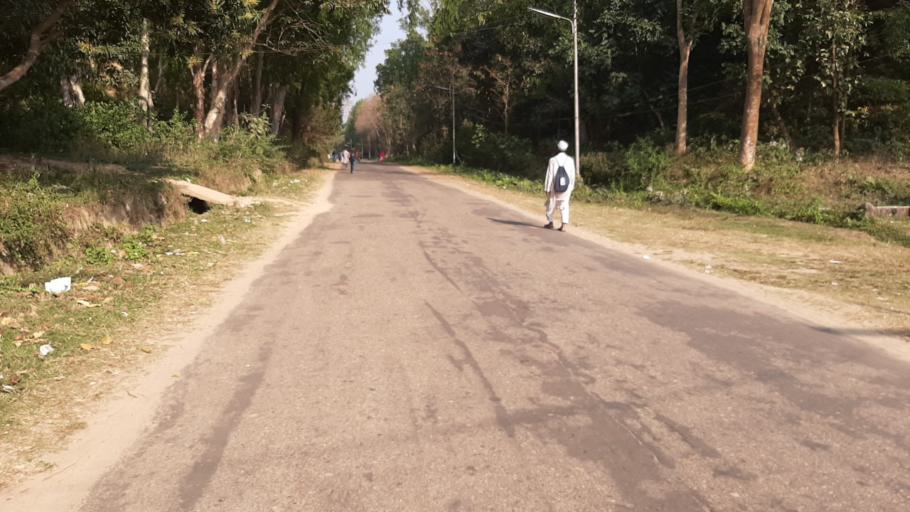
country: BD
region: Chittagong
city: Chittagong
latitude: 22.4743
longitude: 91.7892
